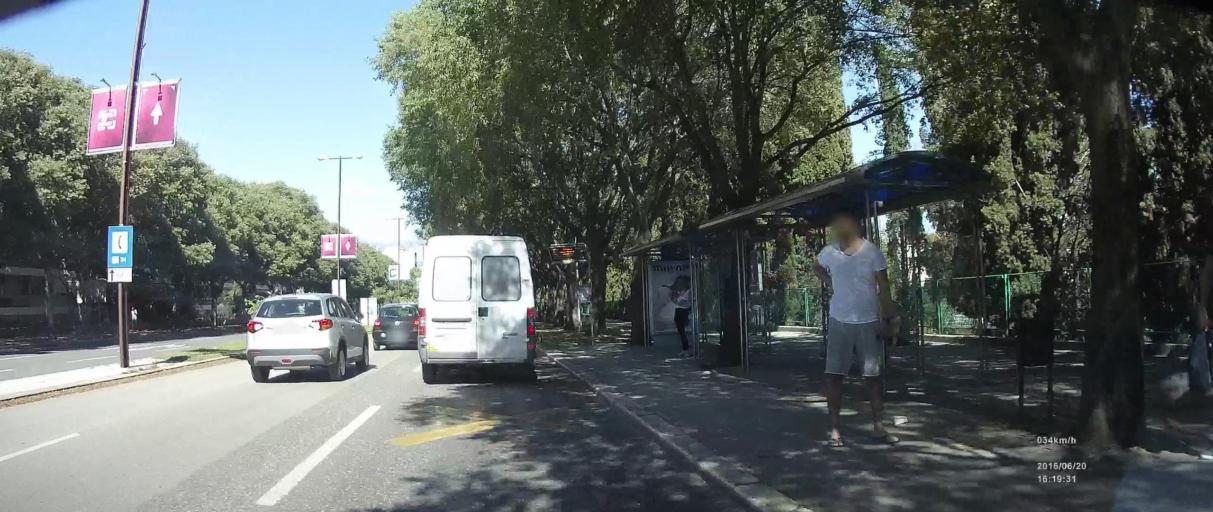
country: HR
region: Splitsko-Dalmatinska
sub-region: Grad Split
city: Split
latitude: 43.5052
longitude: 16.4569
